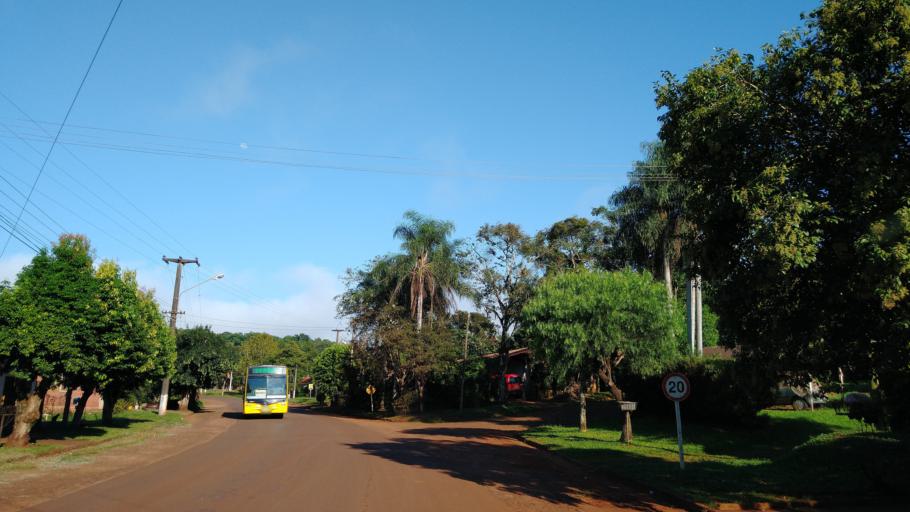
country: AR
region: Misiones
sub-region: Departamento de Montecarlo
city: Montecarlo
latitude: -26.5609
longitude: -54.7792
